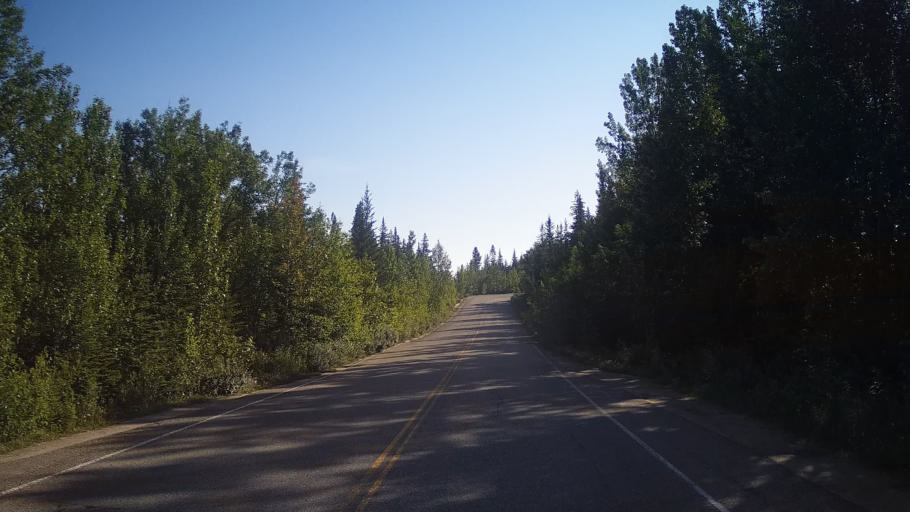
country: CA
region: Alberta
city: Jasper Park Lodge
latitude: 53.2044
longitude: -117.9249
